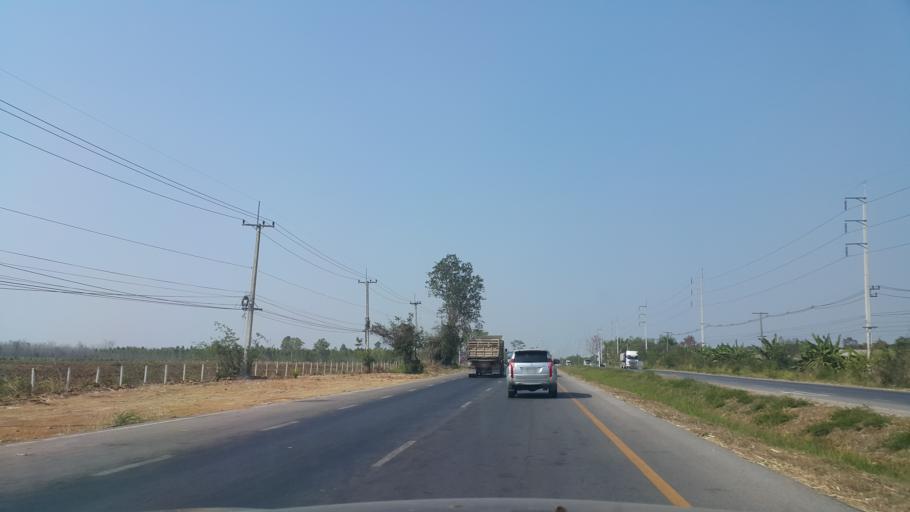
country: TH
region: Chaiyaphum
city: Phu Khiao
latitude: 16.4347
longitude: 102.1274
